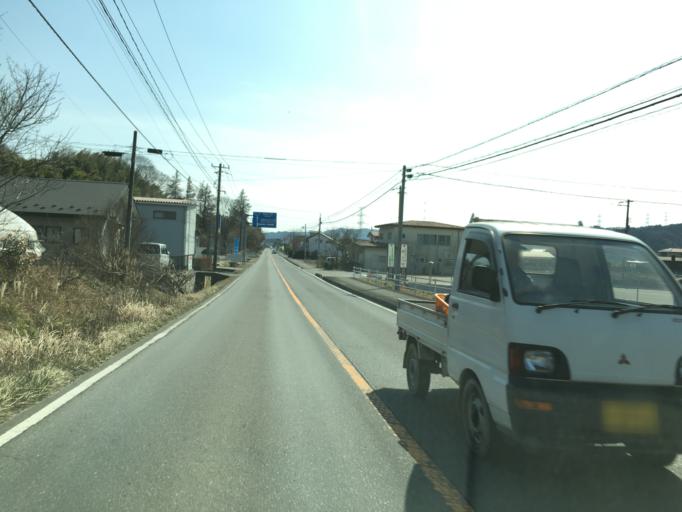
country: JP
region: Ibaraki
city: Daigo
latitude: 36.9070
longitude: 140.4178
